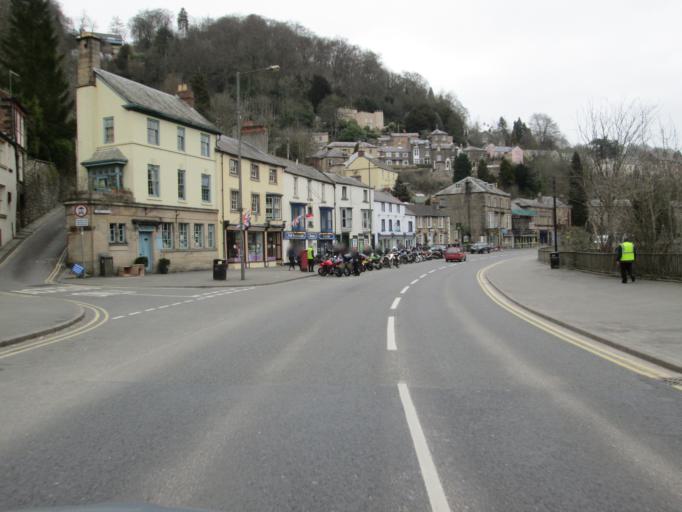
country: GB
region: England
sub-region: Derbyshire
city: Cromford
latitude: 53.1203
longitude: -1.5634
